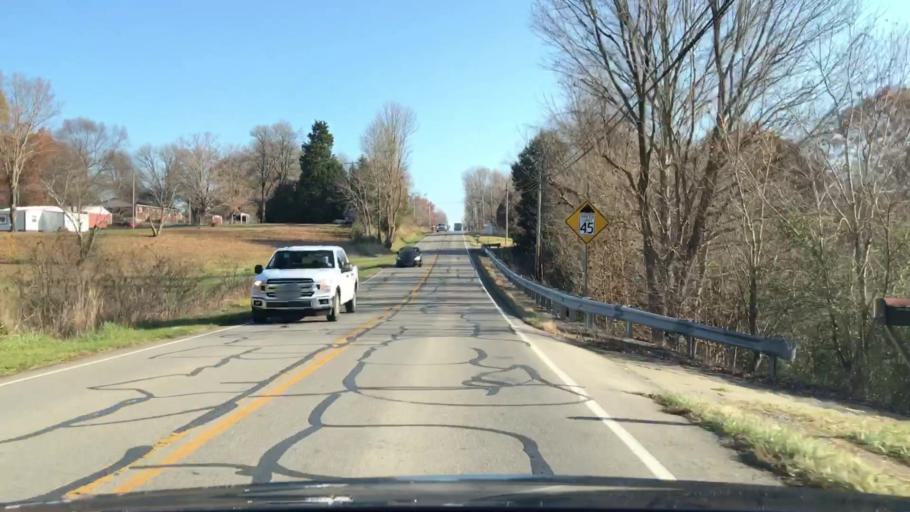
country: US
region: Kentucky
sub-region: Edmonson County
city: Brownsville
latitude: 37.2370
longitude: -86.2928
